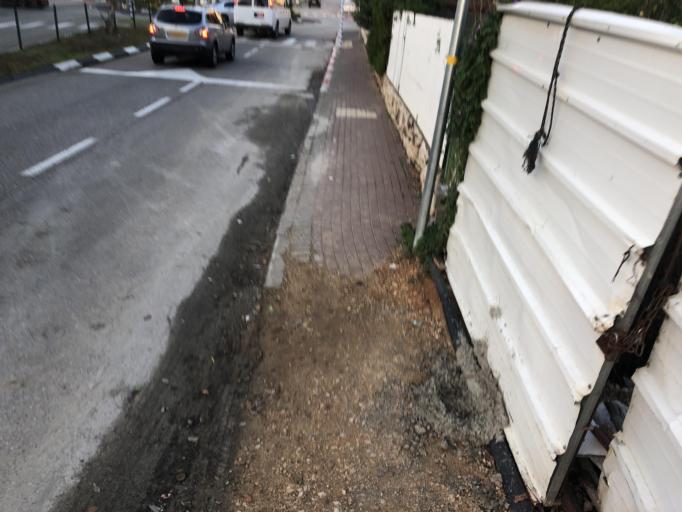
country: IL
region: Northern District
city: `Akko
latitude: 32.9274
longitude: 35.0925
